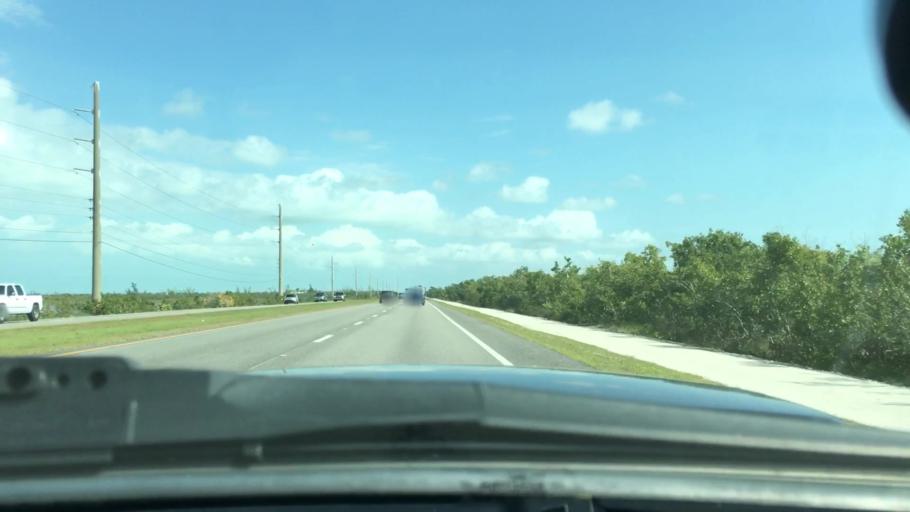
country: US
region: Florida
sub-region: Monroe County
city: Stock Island
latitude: 24.5811
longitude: -81.7047
